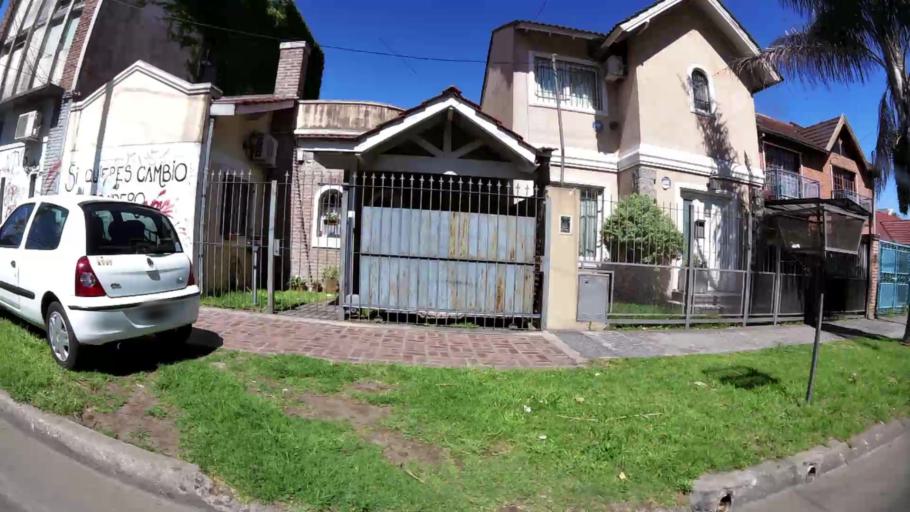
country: AR
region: Buenos Aires
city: Ituzaingo
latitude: -34.6617
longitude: -58.6632
